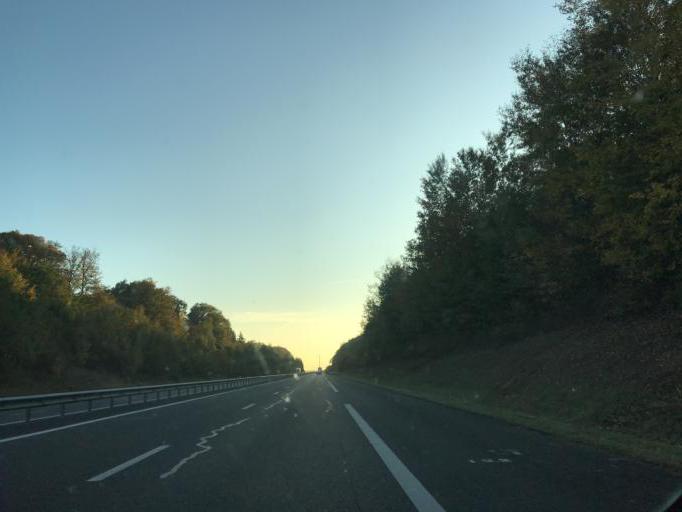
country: FR
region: Bourgogne
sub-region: Departement de l'Yonne
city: Paron
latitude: 48.1938
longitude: 3.1921
